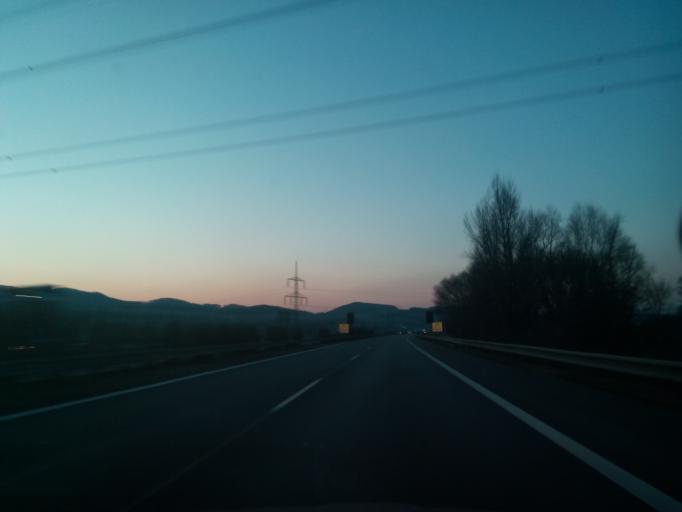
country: SK
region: Presovsky
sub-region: Okres Presov
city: Presov
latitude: 48.8599
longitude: 21.2654
